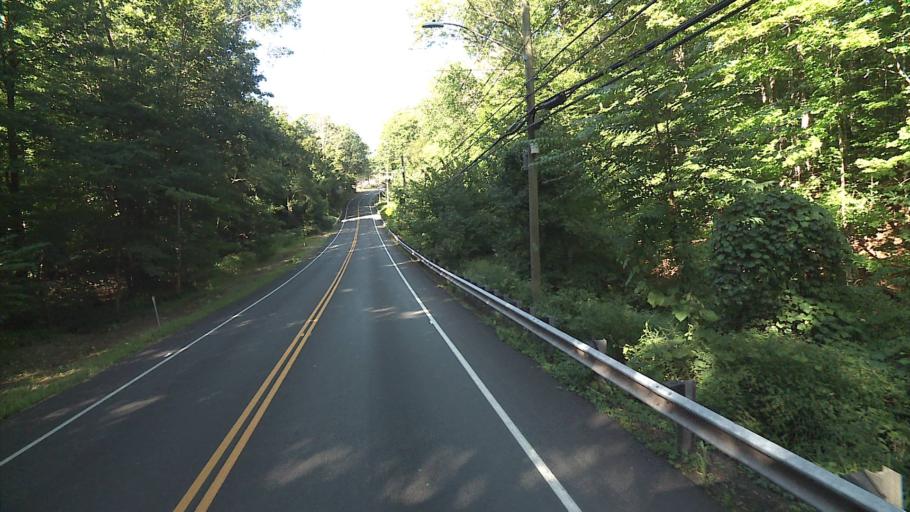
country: US
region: Connecticut
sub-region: New Haven County
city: Cheshire
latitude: 41.4990
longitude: -72.8966
